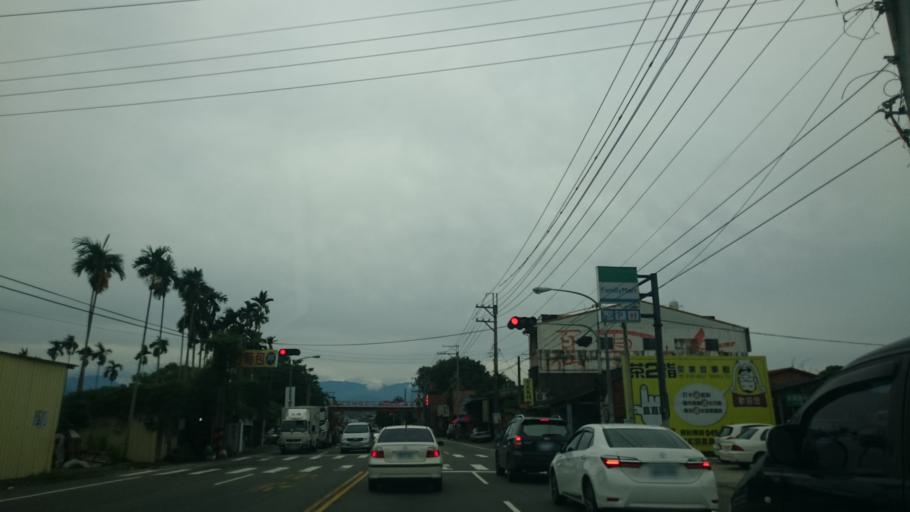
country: TW
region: Taiwan
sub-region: Nantou
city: Nantou
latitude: 23.8470
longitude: 120.6976
